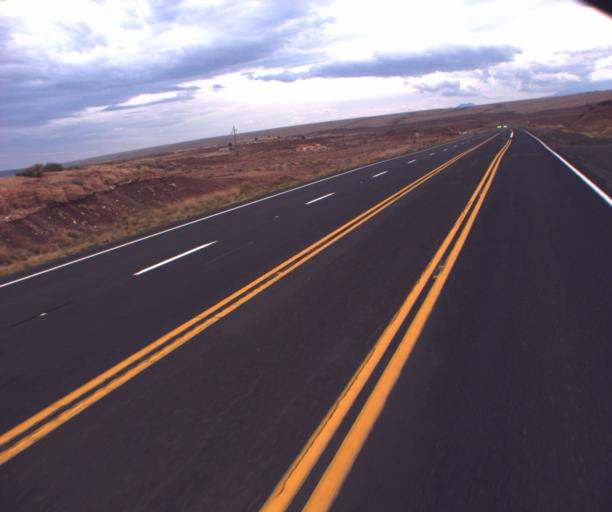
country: US
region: Arizona
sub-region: Coconino County
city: Tuba City
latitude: 35.7988
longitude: -111.4472
